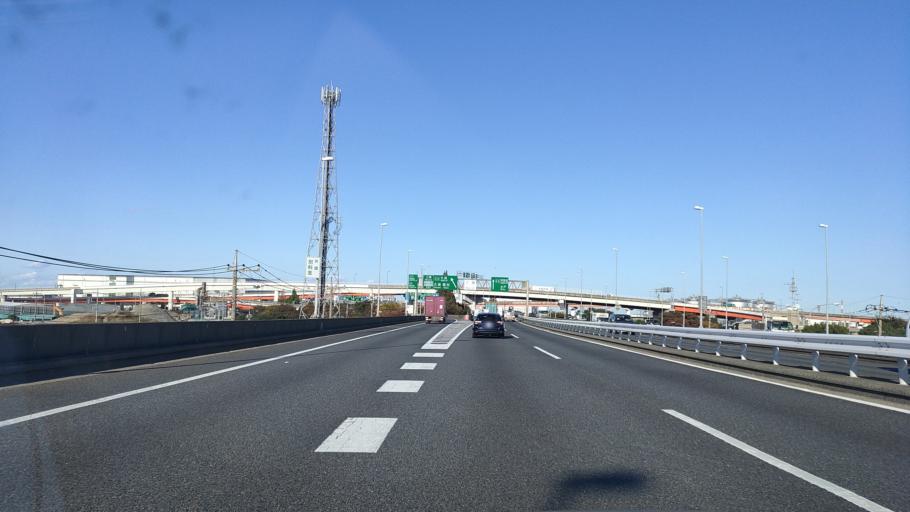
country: JP
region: Saitama
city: Yashio-shi
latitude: 35.8316
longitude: 139.8588
